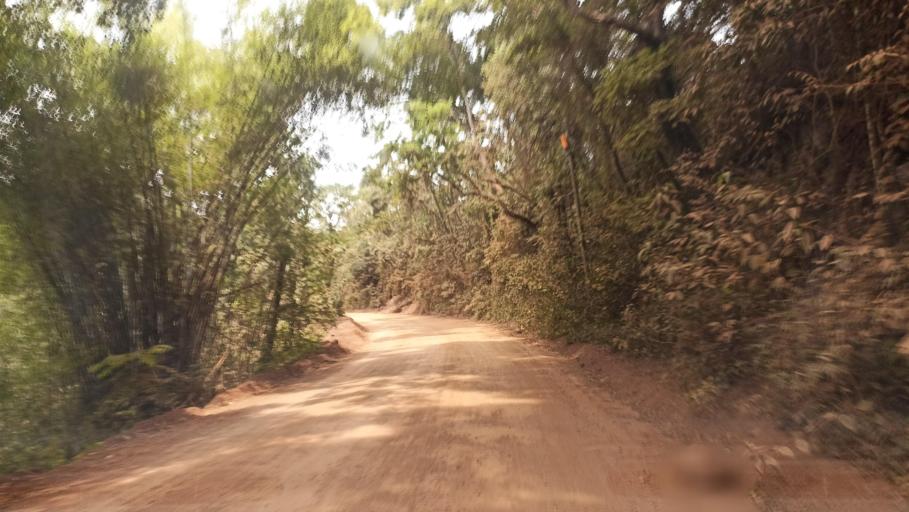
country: BR
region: Minas Gerais
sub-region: Itabirito
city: Itabirito
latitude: -20.3647
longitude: -43.7626
